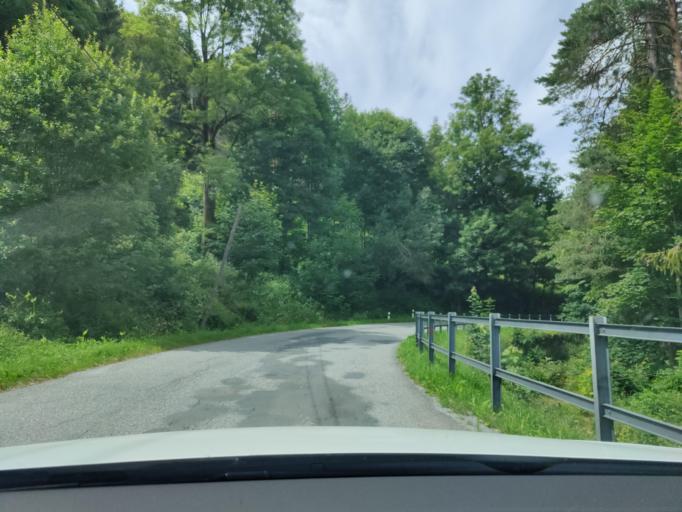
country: CZ
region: Olomoucky
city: Zlate Hory
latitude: 50.2236
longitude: 17.3450
